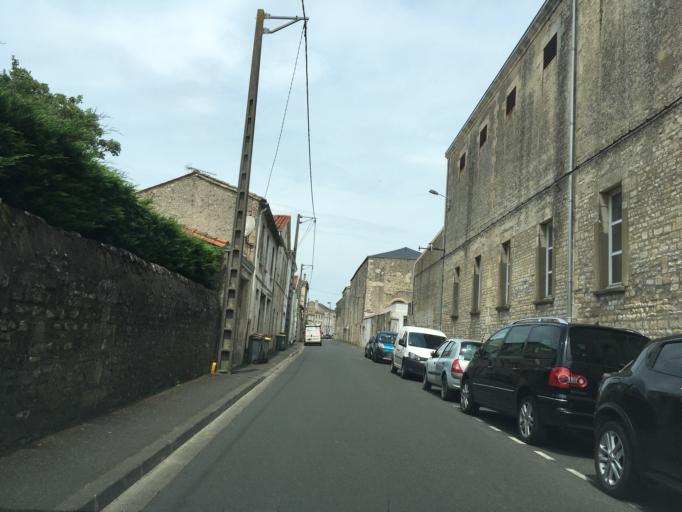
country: FR
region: Poitou-Charentes
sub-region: Departement des Deux-Sevres
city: Niort
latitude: 46.3181
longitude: -0.4648
